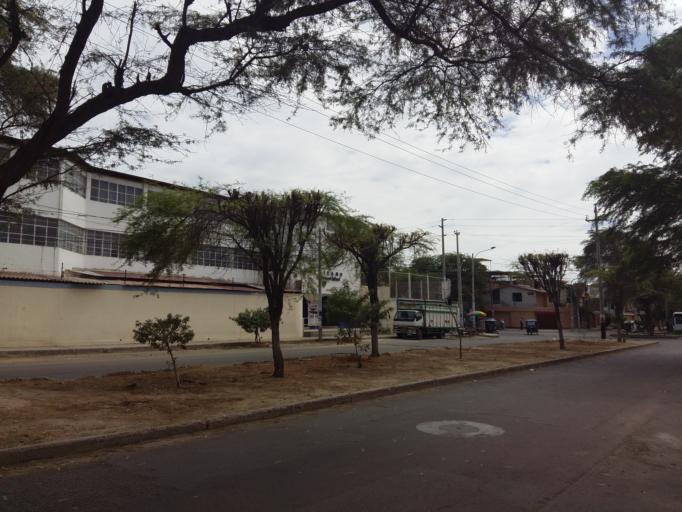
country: PE
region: Piura
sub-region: Provincia de Piura
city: Piura
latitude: -5.1884
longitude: -80.6186
